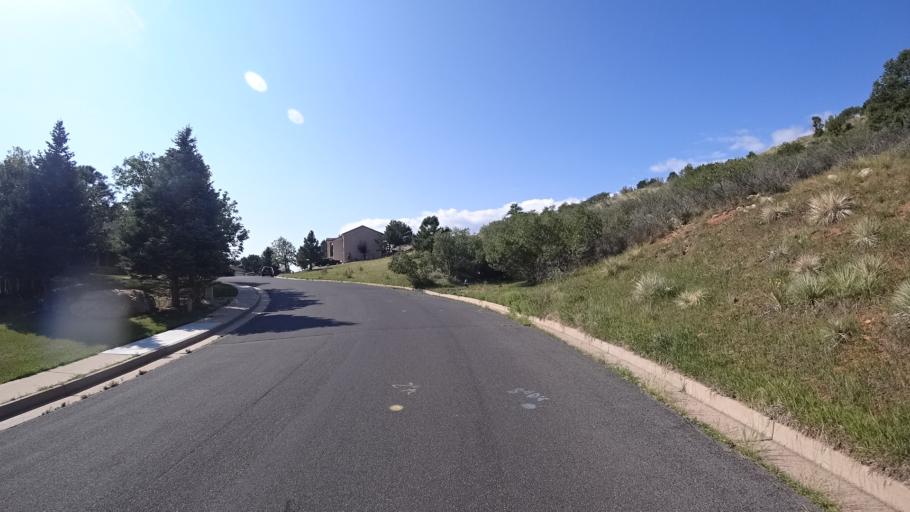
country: US
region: Colorado
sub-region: El Paso County
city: Manitou Springs
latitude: 38.9103
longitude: -104.8767
